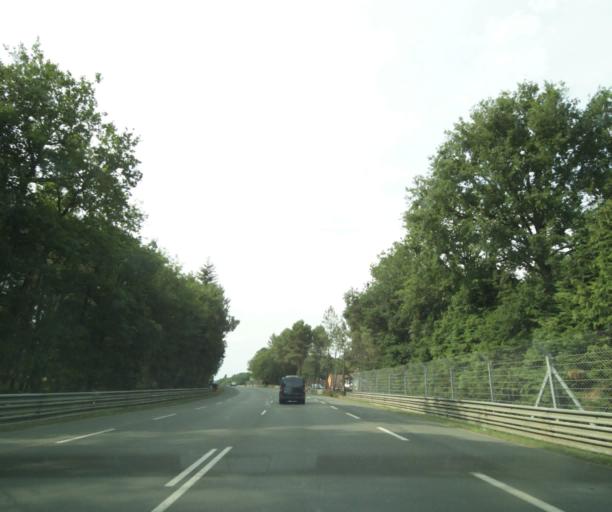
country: FR
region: Pays de la Loire
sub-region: Departement de la Sarthe
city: Mulsanne
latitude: 47.9243
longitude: 0.2431
